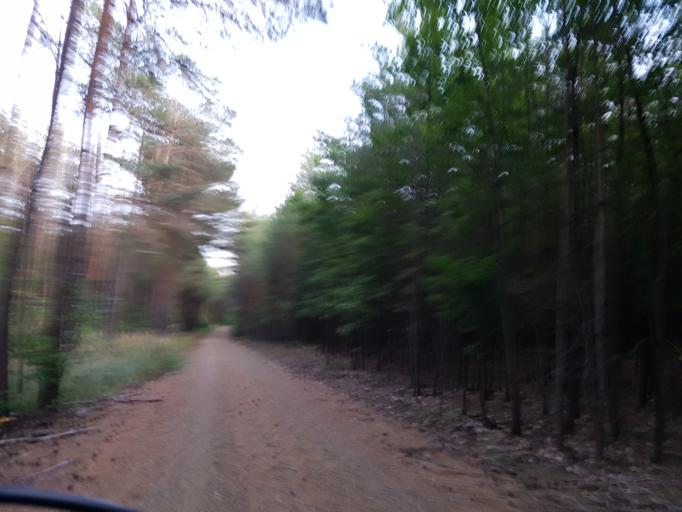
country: DE
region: Brandenburg
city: Trobitz
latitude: 51.5650
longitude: 13.4471
